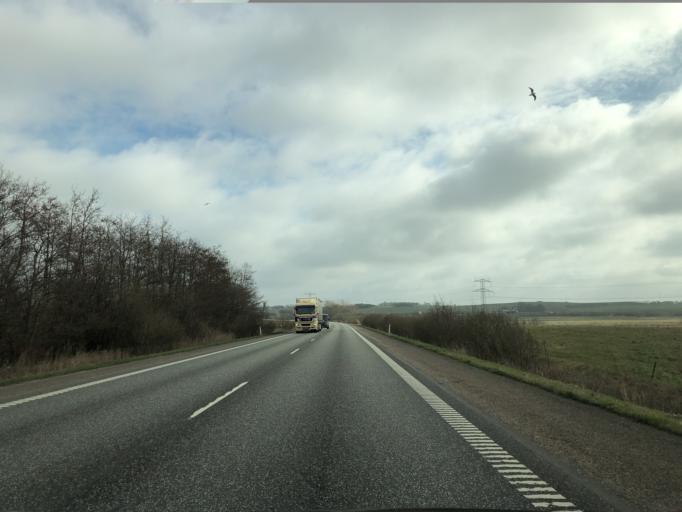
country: DK
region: North Denmark
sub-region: Rebild Kommune
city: Stovring
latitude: 56.8223
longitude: 9.7076
